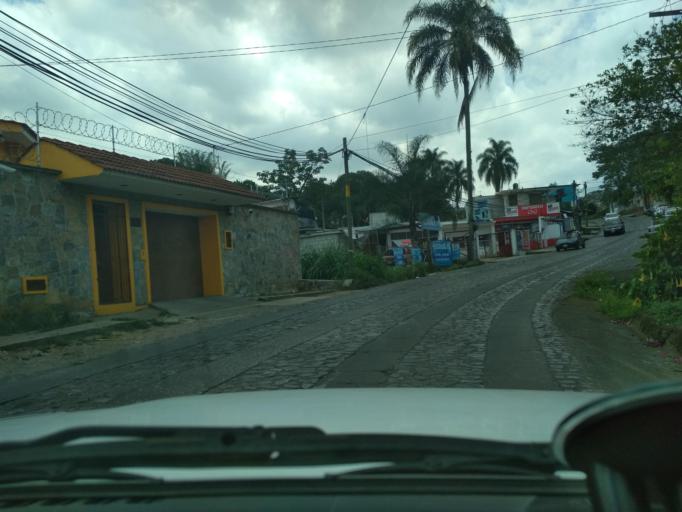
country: MX
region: Veracruz
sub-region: Cordoba
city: San Jose de Abajo [Unidad Habitacional]
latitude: 18.9098
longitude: -96.9602
